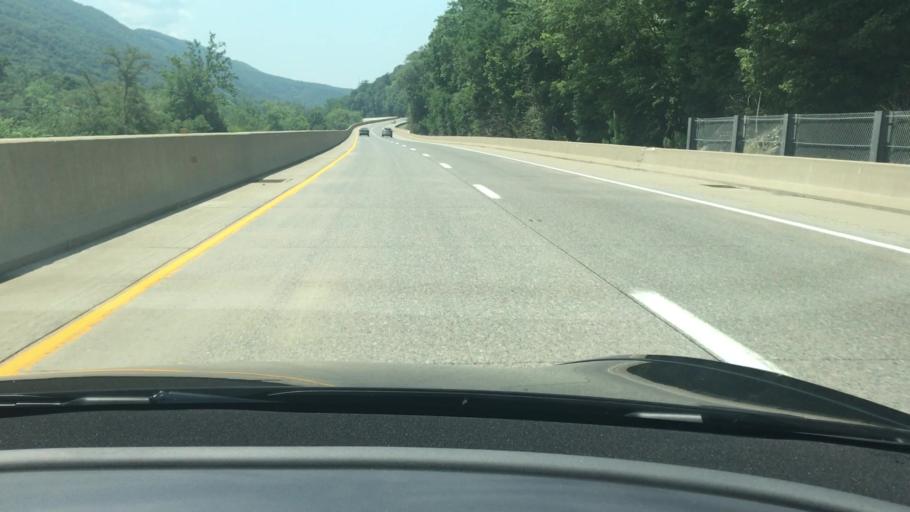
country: US
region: Pennsylvania
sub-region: Mifflin County
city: Lewistown
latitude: 40.5927
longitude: -77.5107
